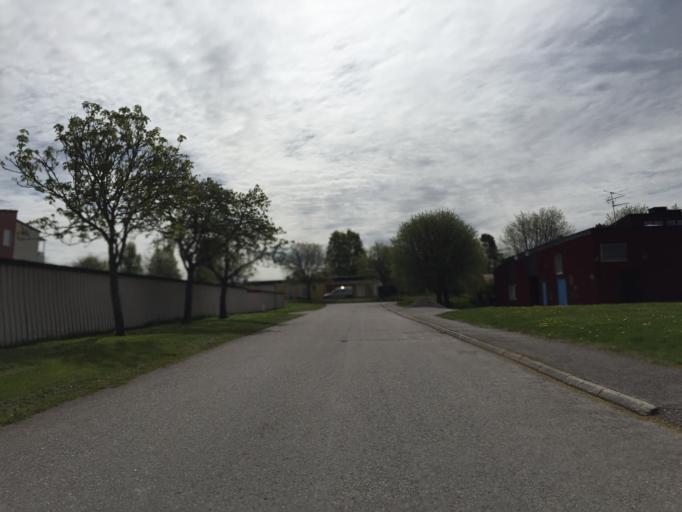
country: SE
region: Dalarna
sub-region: Ludvika Kommun
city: Ludvika
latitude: 60.1310
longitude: 15.1834
